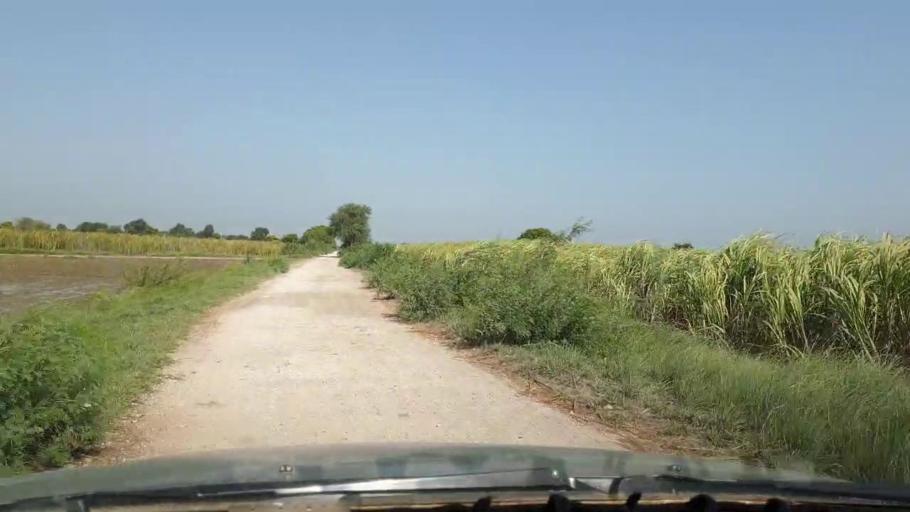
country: PK
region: Sindh
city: Matli
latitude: 25.0853
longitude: 68.6131
